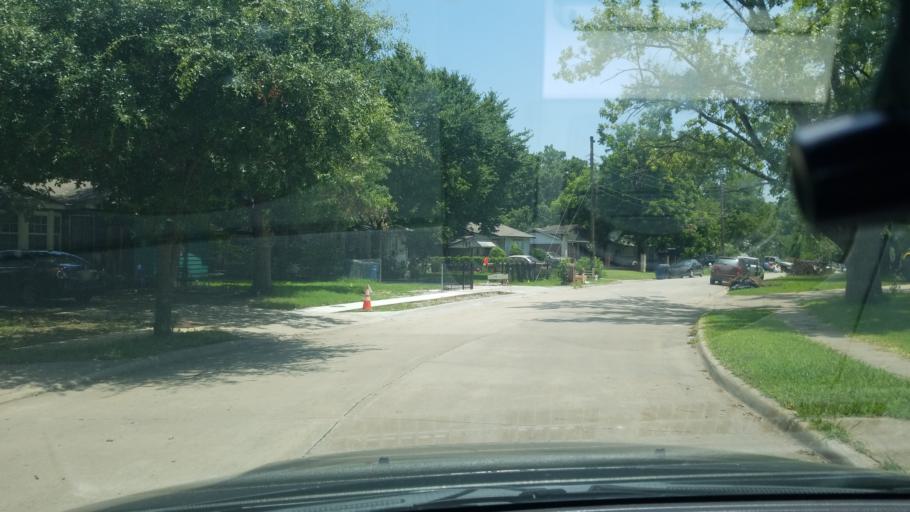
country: US
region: Texas
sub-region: Dallas County
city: Balch Springs
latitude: 32.7313
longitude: -96.6641
